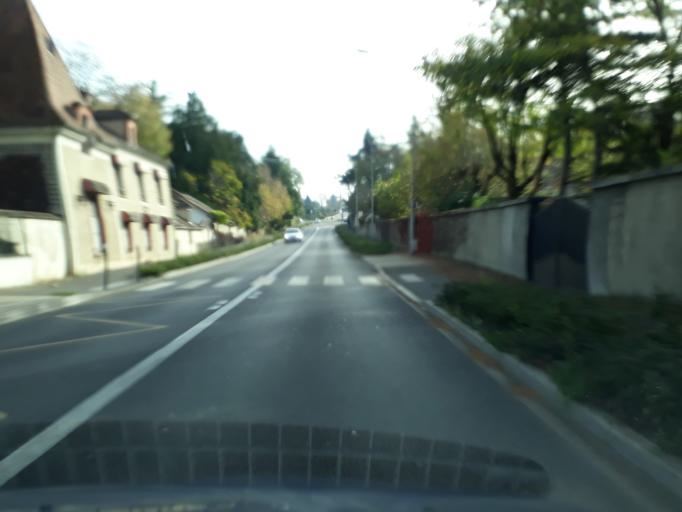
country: FR
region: Ile-de-France
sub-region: Departement de Seine-et-Marne
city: Samoreau
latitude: 48.4294
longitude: 2.7480
